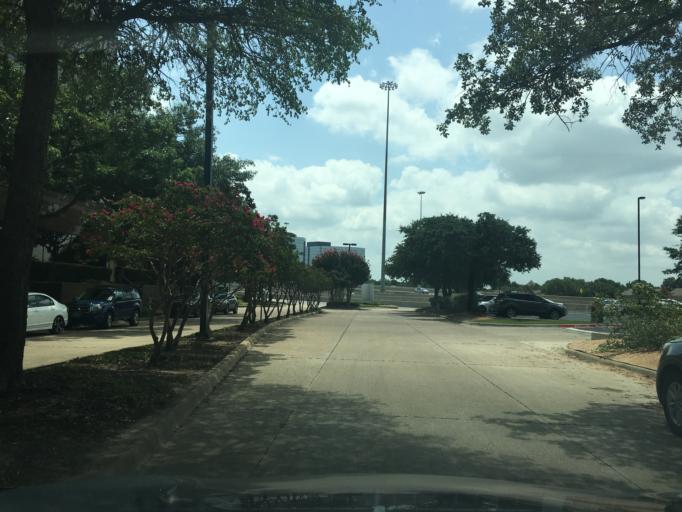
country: US
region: Texas
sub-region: Dallas County
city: Addison
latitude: 32.9272
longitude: -96.8243
